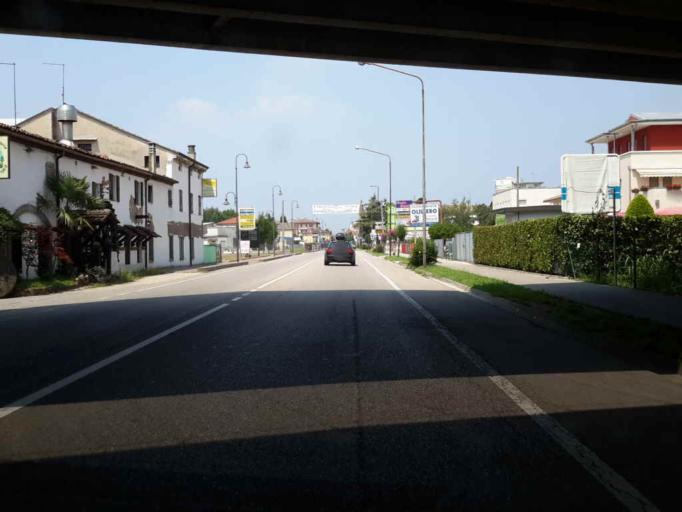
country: IT
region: Veneto
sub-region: Provincia di Vicenza
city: Torri di Quartesolo
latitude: 45.5160
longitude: 11.6222
